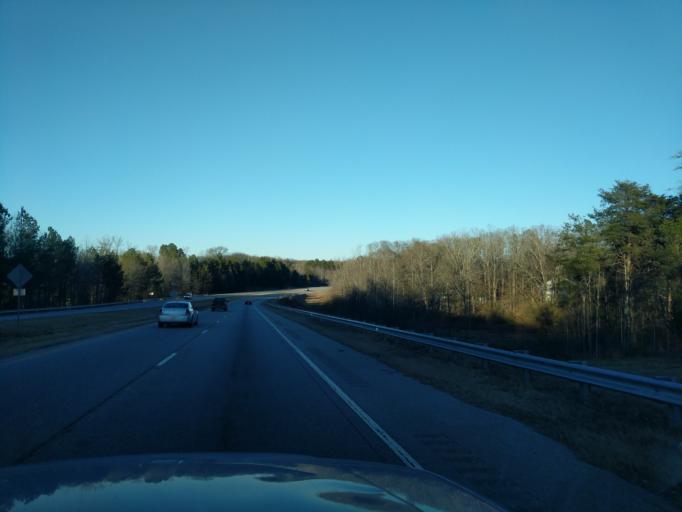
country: US
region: Georgia
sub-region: Stephens County
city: Toccoa
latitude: 34.5381
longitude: -83.2966
